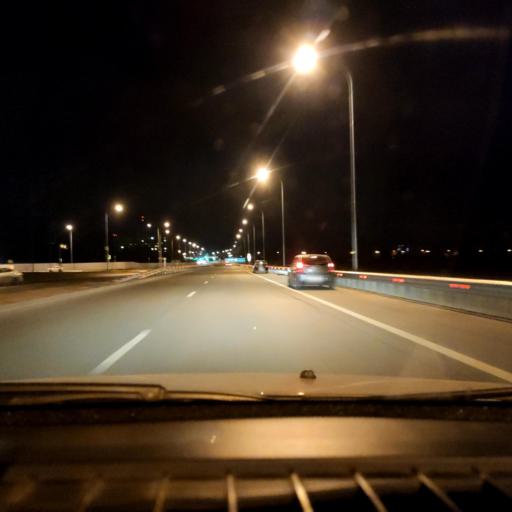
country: RU
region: Samara
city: Bereza
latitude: 53.5149
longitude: 50.1533
